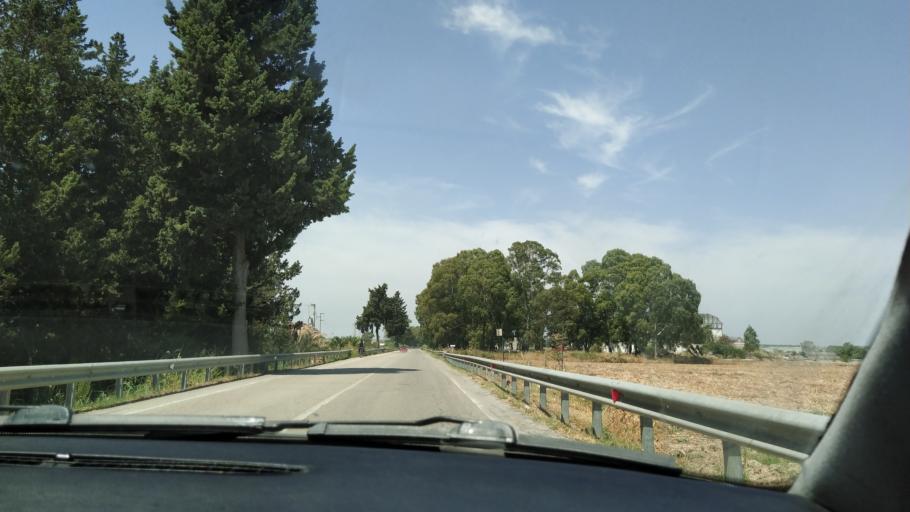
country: IT
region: Apulia
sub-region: Provincia di Taranto
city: Marina di Ginosa
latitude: 40.3745
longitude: 16.7985
